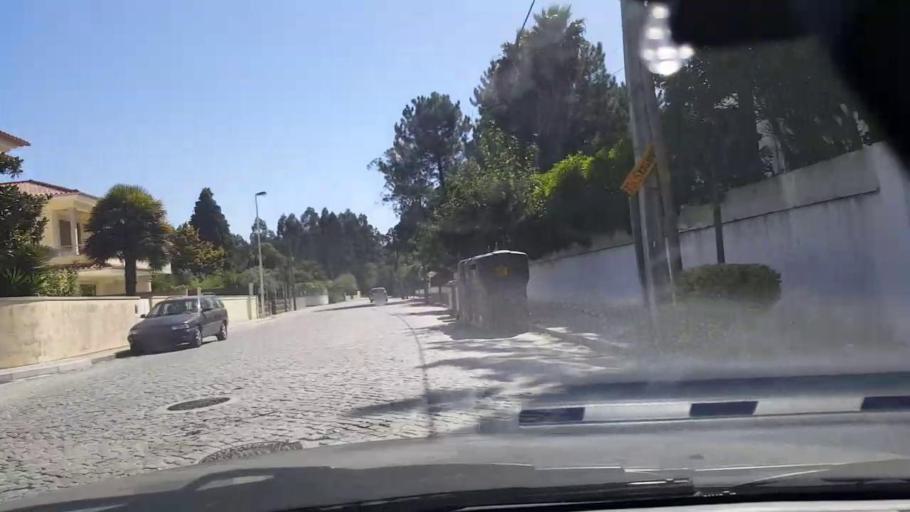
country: PT
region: Porto
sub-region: Vila do Conde
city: Arvore
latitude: 41.3296
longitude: -8.7290
